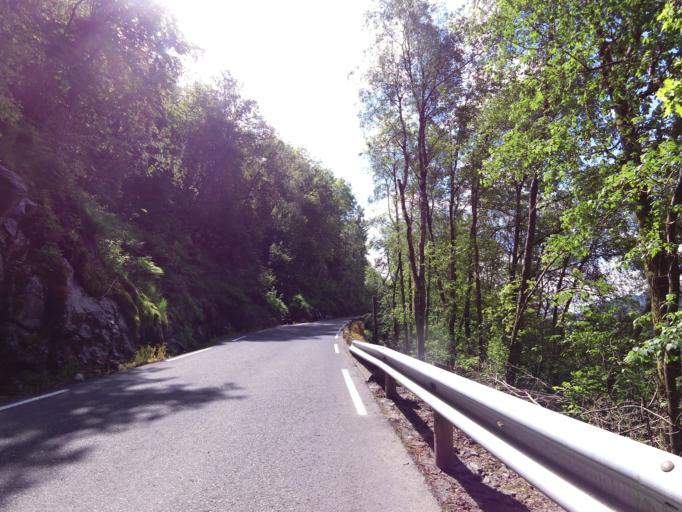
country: NO
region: Vest-Agder
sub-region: Kvinesdal
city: Liknes
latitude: 58.2979
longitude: 6.9501
